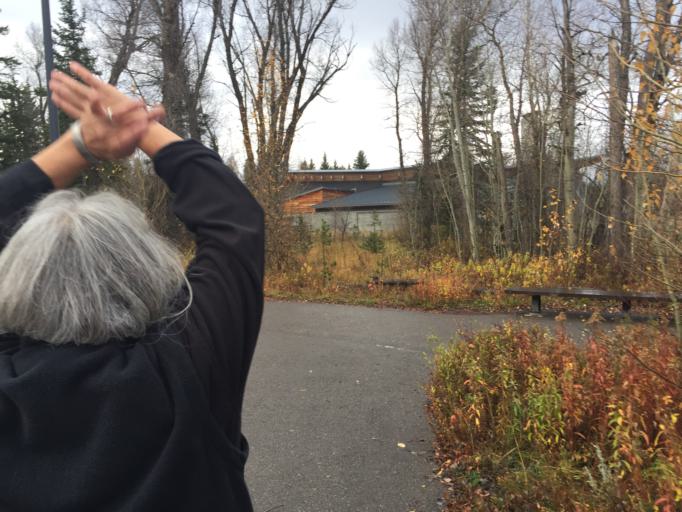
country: US
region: Wyoming
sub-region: Teton County
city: Jackson
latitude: 43.6541
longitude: -110.7177
